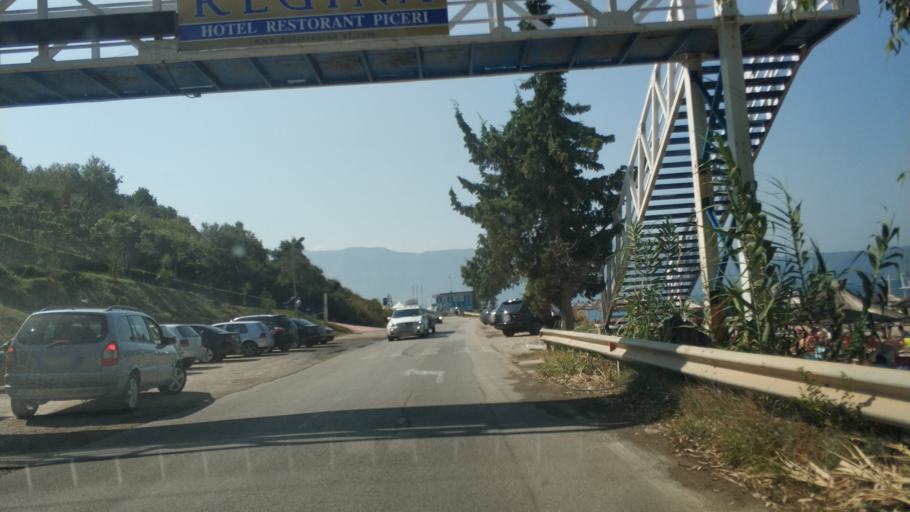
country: AL
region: Vlore
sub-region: Rrethi i Vlores
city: Orikum
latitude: 40.3628
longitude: 19.4804
